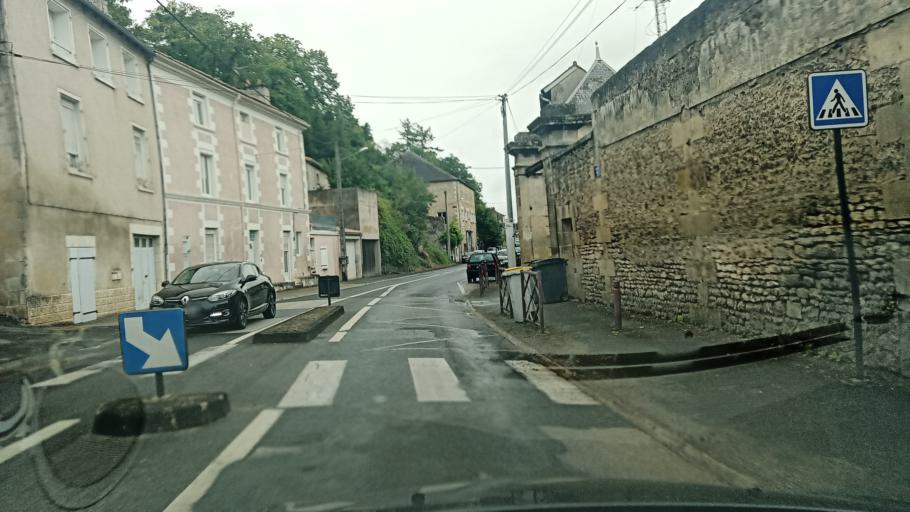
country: FR
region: Poitou-Charentes
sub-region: Departement de la Vienne
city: Poitiers
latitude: 46.6058
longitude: 0.3449
